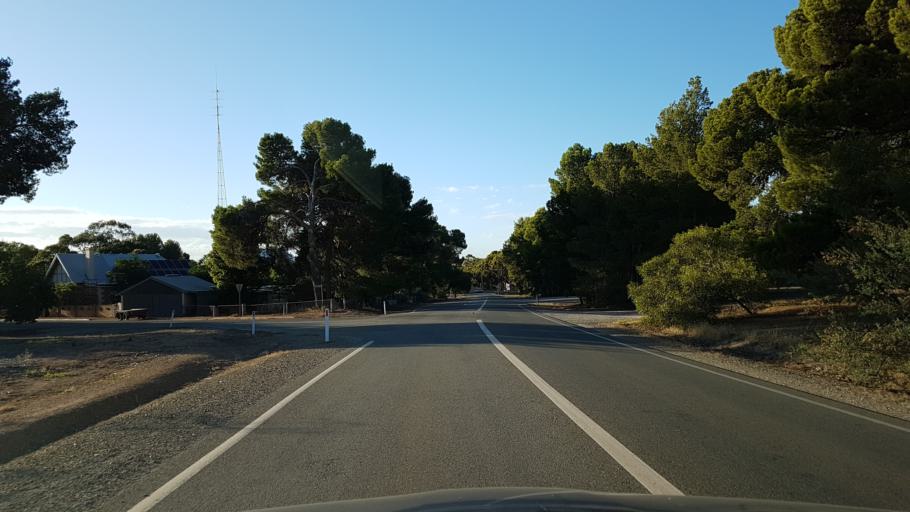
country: AU
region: South Australia
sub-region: Port Pirie City and Dists
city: Crystal Brook
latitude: -33.2702
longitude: 138.3518
